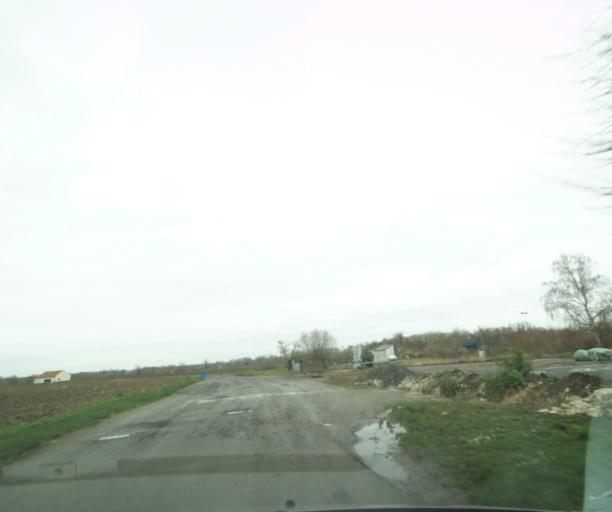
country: FR
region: Picardie
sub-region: Departement de l'Oise
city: Noyon
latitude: 49.5736
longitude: 3.0022
